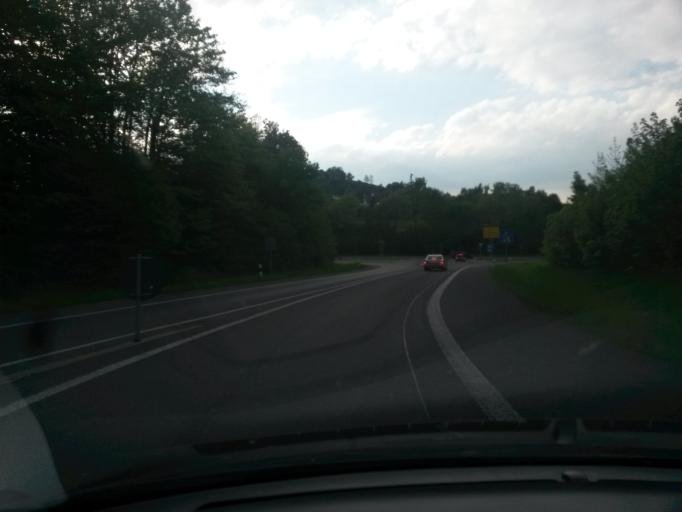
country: DE
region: Hesse
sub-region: Regierungsbezirk Kassel
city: Martinhagen
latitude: 51.3194
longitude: 9.2833
